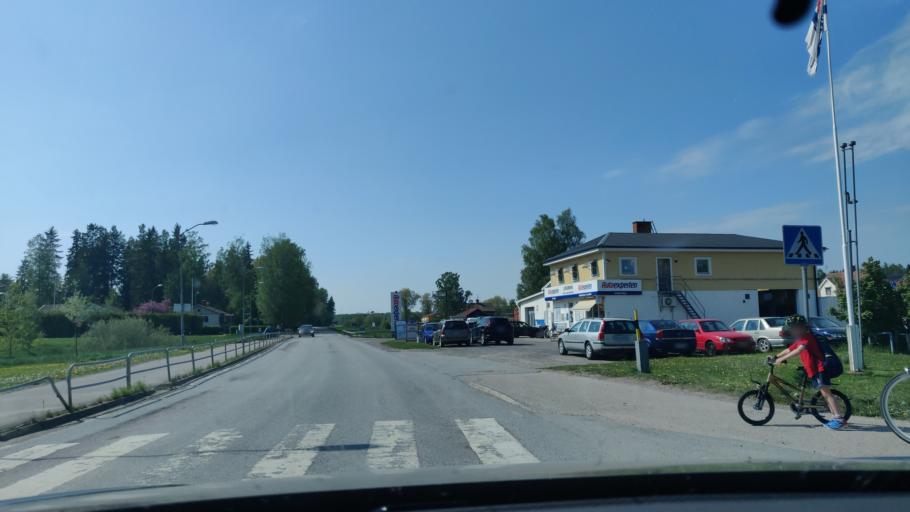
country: SE
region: Uppsala
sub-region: Heby Kommun
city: OEstervala
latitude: 60.1821
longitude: 17.1740
